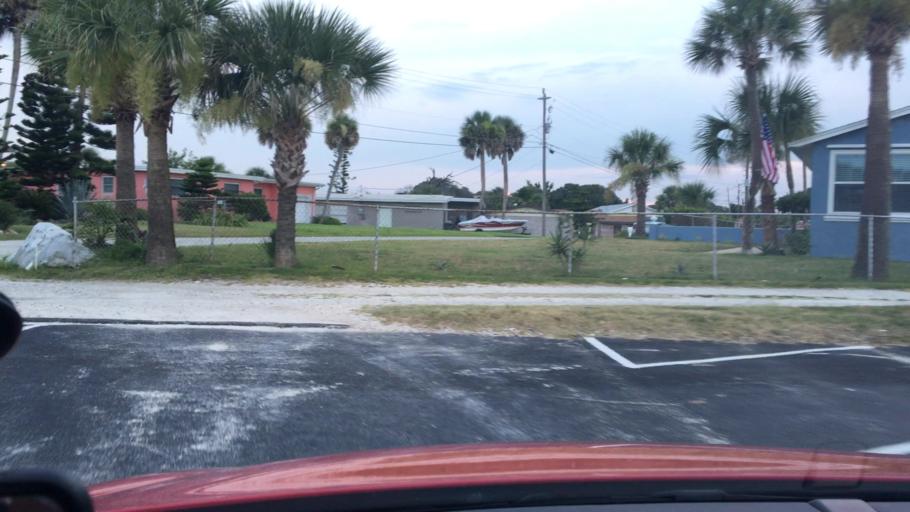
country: US
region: Florida
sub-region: Volusia County
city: Daytona Beach Shores
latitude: 29.1950
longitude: -80.9930
